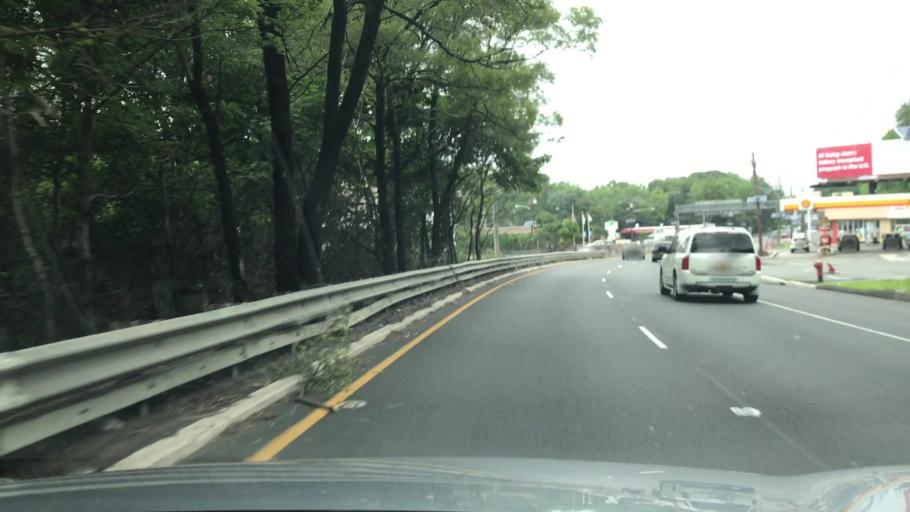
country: US
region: New Jersey
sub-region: Bergen County
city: Leonia
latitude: 40.8655
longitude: -73.9739
